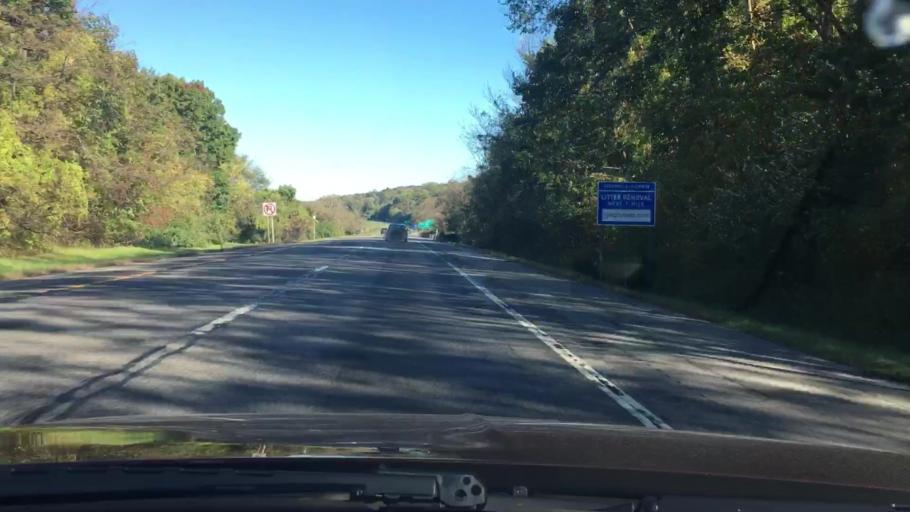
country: US
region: New York
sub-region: Putnam County
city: Peach Lake
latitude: 41.3838
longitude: -73.5681
